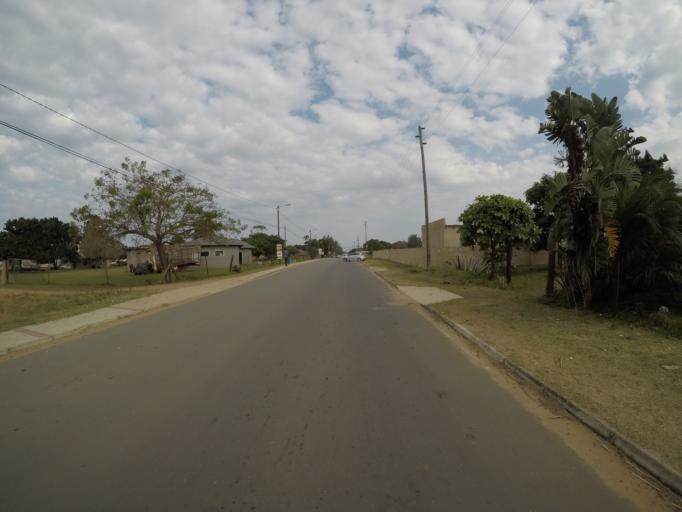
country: ZA
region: KwaZulu-Natal
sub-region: uThungulu District Municipality
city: Richards Bay
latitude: -28.7381
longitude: 32.1013
